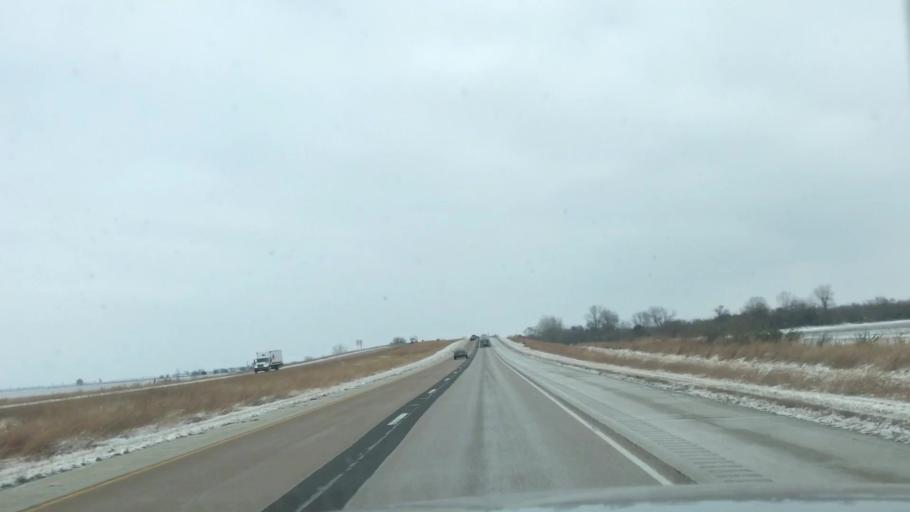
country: US
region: Illinois
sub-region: Montgomery County
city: Litchfield
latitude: 39.1923
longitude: -89.6689
